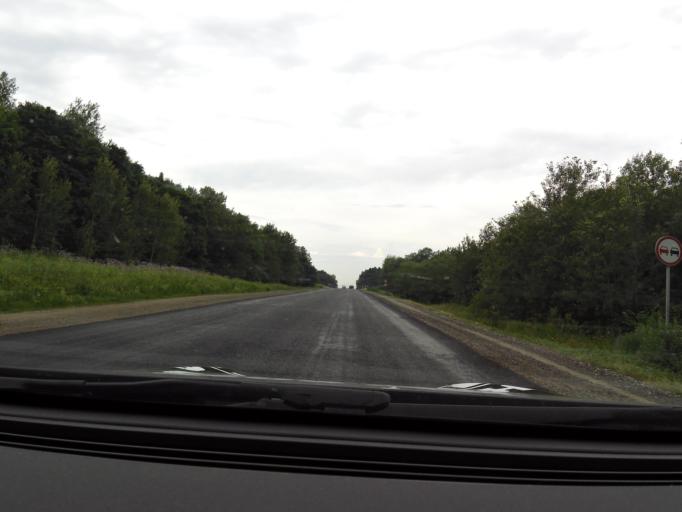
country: RU
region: Bashkortostan
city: Iglino
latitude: 54.7712
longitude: 56.4573
